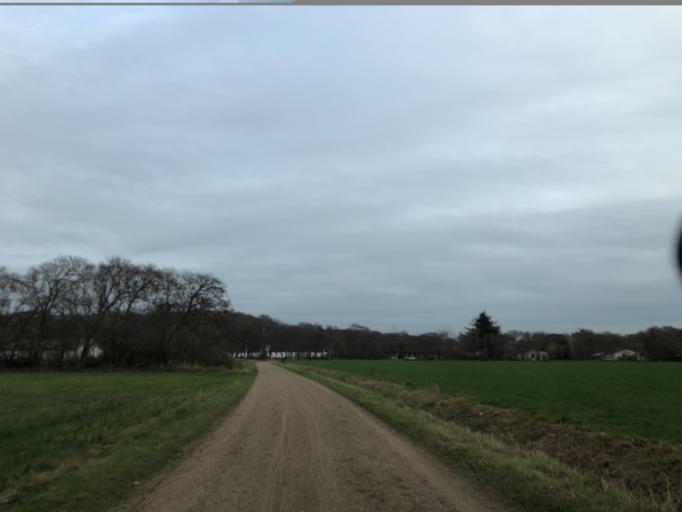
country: DK
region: Central Jutland
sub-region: Holstebro Kommune
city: Ulfborg
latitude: 56.2775
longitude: 8.2304
